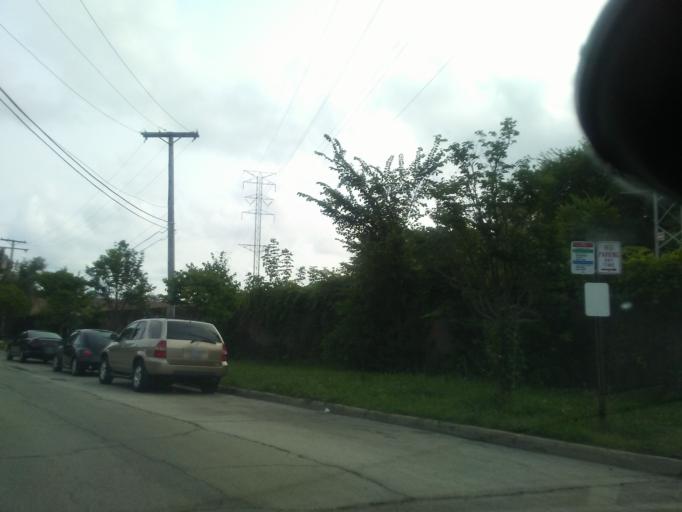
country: US
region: Illinois
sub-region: Cook County
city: Evanston
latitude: 42.0471
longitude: -87.6977
